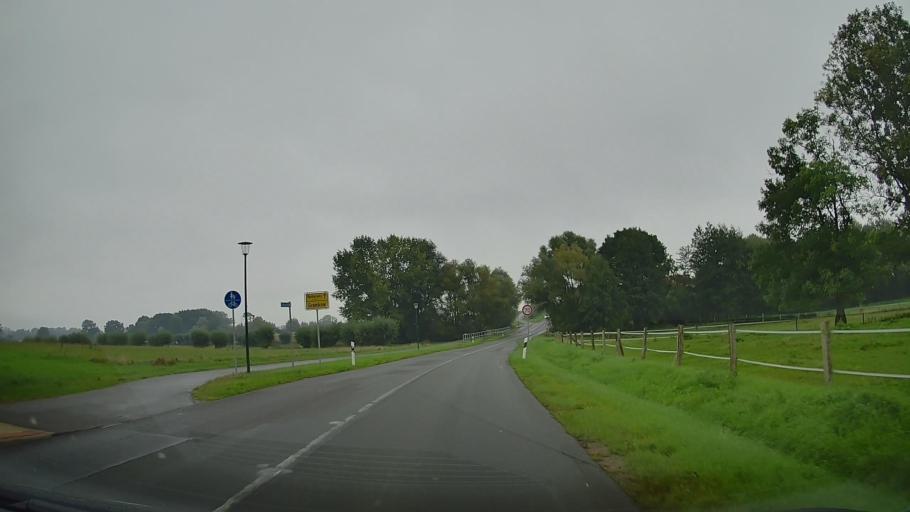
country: DE
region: Mecklenburg-Vorpommern
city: Gramkow
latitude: 53.9228
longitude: 11.3163
